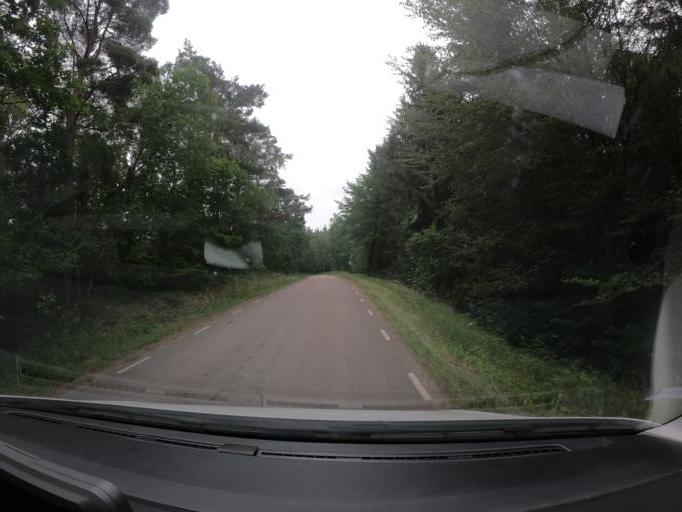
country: SE
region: Skane
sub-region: Perstorps Kommun
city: Perstorp
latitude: 56.0881
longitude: 13.3214
